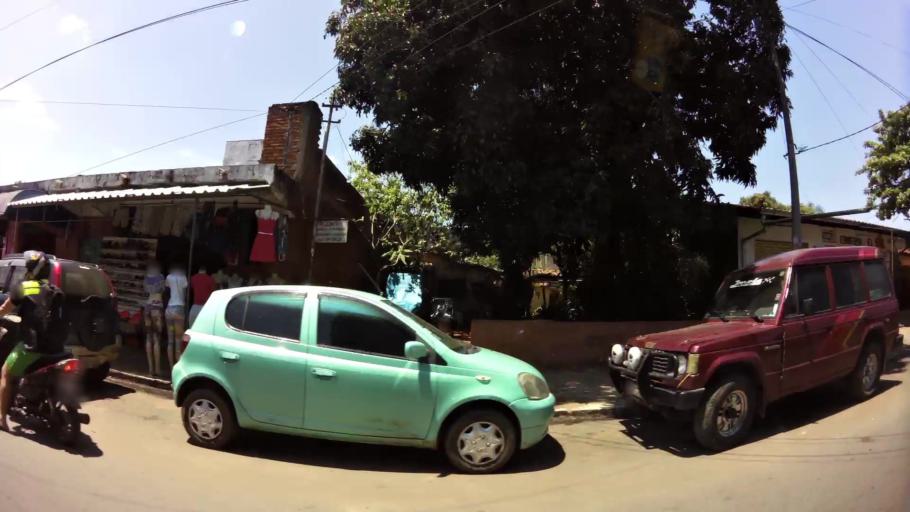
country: PY
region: Central
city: Nemby
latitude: -25.3955
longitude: -57.5463
